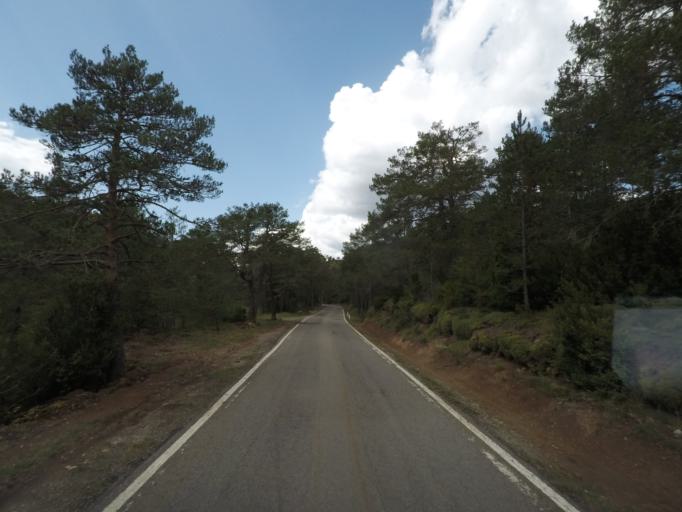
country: ES
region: Aragon
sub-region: Provincia de Huesca
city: Fiscal
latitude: 42.4053
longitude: -0.1729
